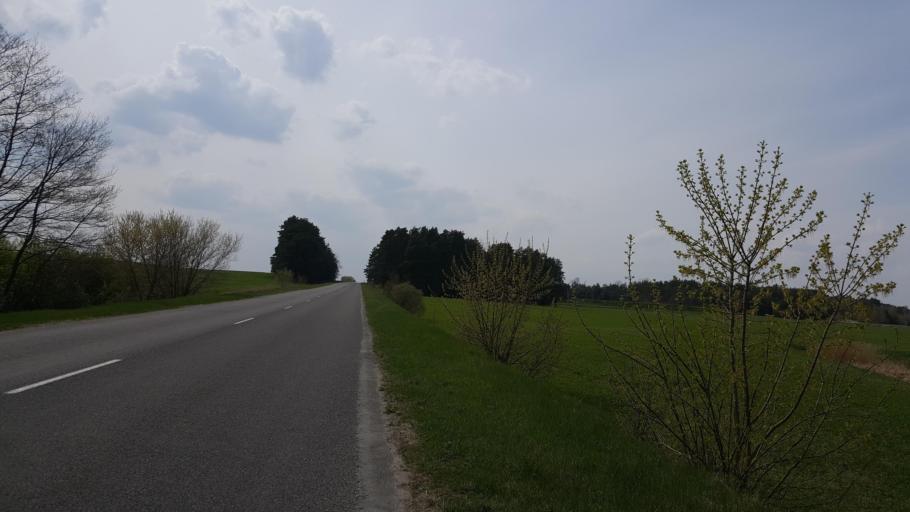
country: BY
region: Brest
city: Zhabinka
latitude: 52.2089
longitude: 23.9331
